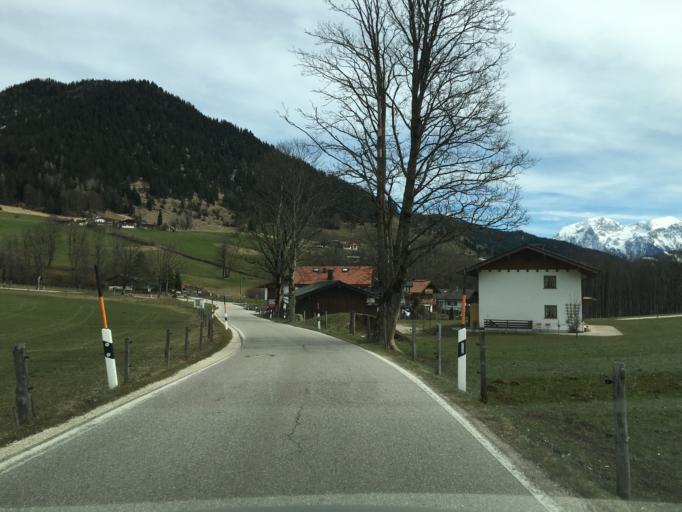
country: DE
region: Bavaria
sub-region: Upper Bavaria
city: Ramsau
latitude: 47.6149
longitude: 12.8740
